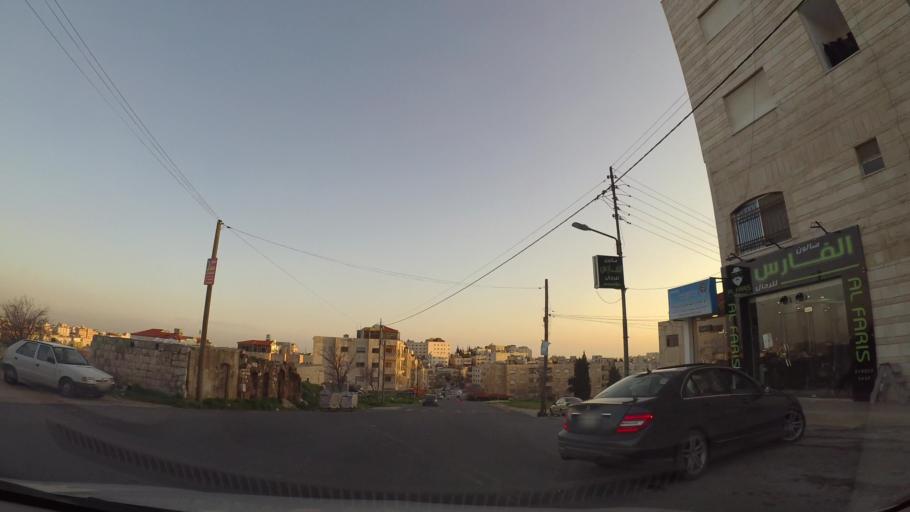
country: JO
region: Amman
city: Al Jubayhah
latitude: 32.0007
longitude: 35.8624
